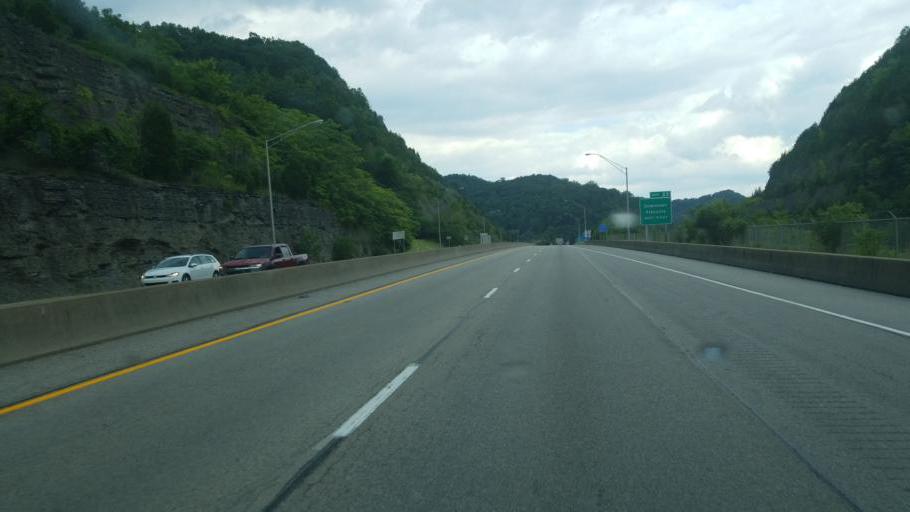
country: US
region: Kentucky
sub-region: Pike County
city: Pikeville
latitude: 37.4773
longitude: -82.5406
